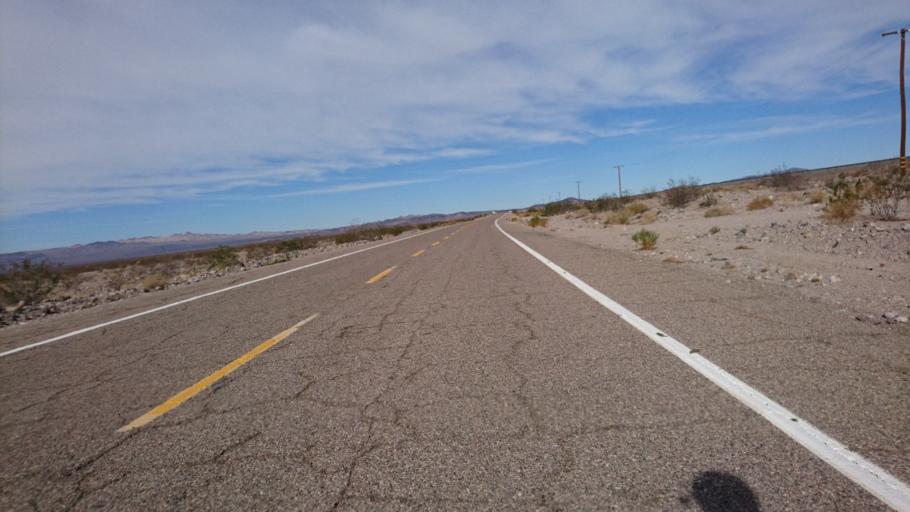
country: US
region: California
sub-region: San Bernardino County
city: Twentynine Palms
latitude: 34.6079
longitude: -115.9657
